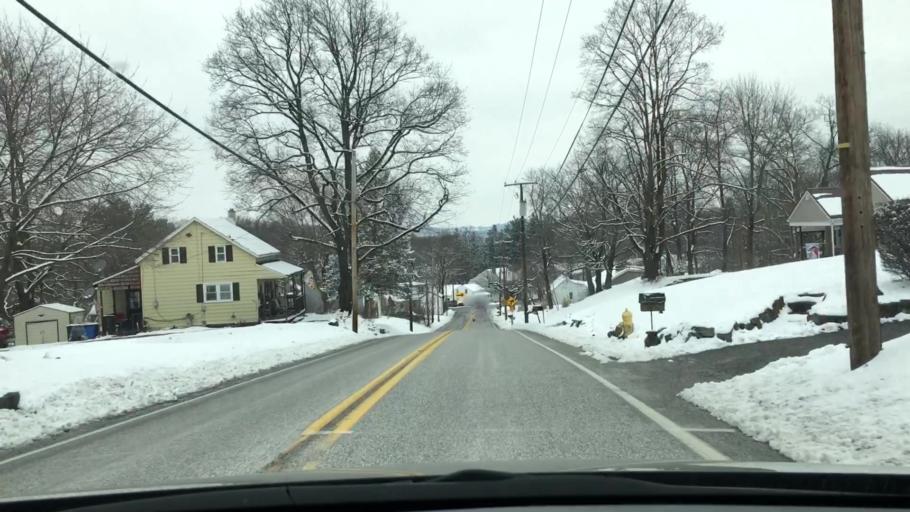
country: US
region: Pennsylvania
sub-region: York County
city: Emigsville
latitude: 39.9997
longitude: -76.7062
